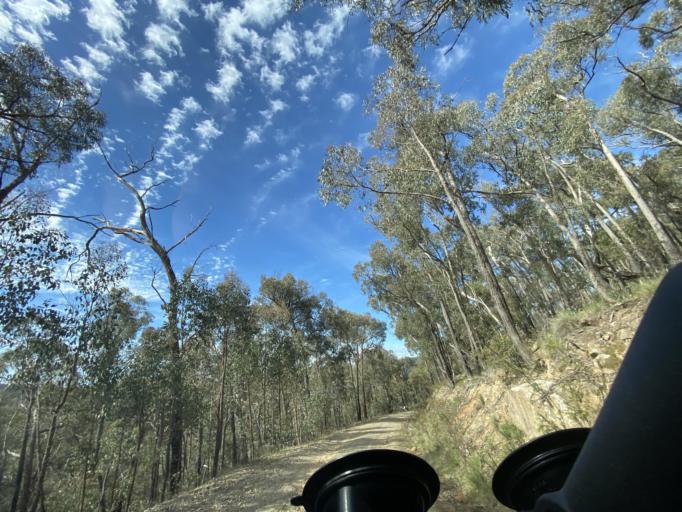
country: AU
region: Victoria
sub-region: Mansfield
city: Mansfield
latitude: -36.8040
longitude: 146.1080
